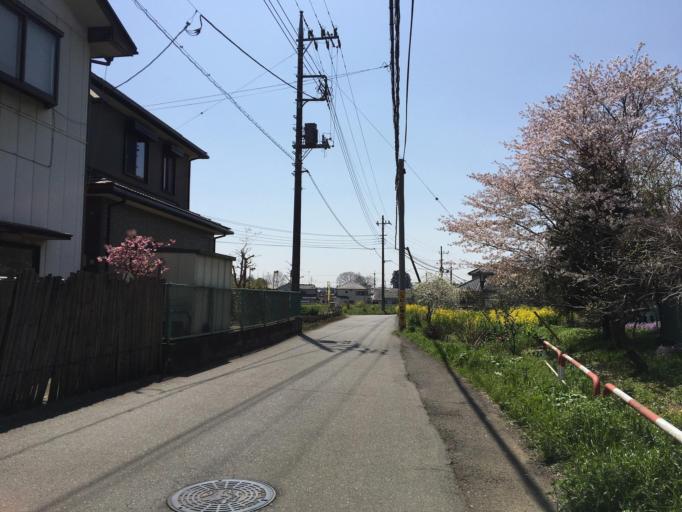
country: JP
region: Saitama
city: Sakado
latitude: 35.9045
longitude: 139.3601
